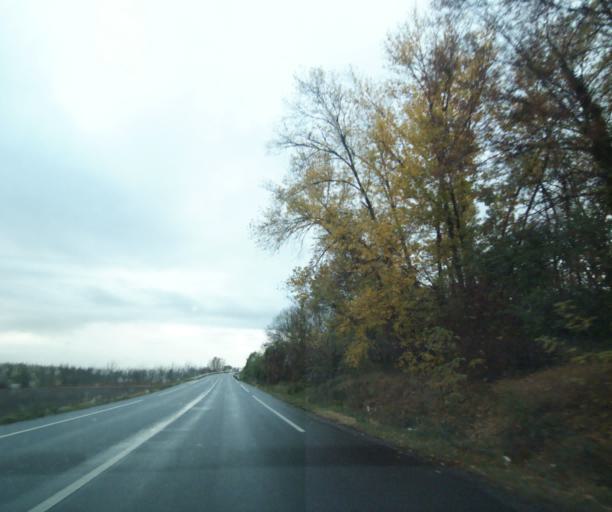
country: FR
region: Auvergne
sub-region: Departement du Puy-de-Dome
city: Aulnat
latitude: 45.7749
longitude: 3.1472
